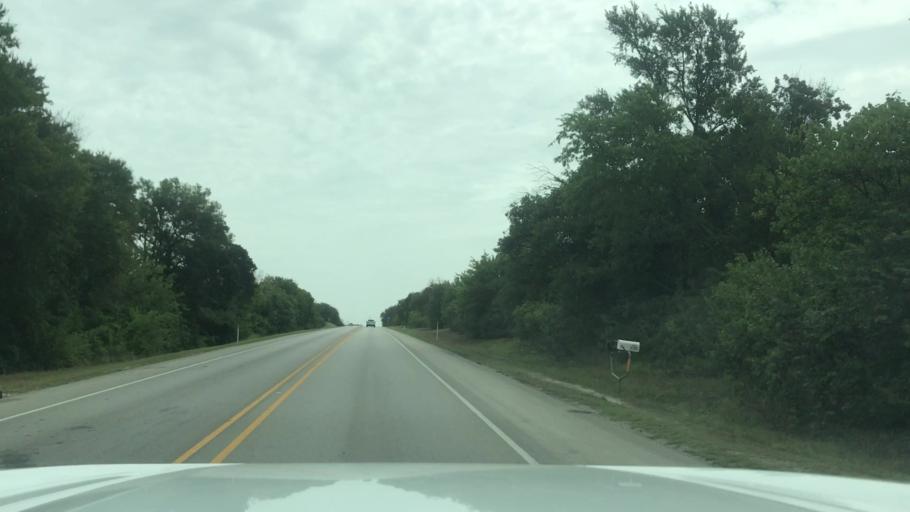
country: US
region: Texas
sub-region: Erath County
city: Dublin
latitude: 32.0984
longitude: -98.3927
